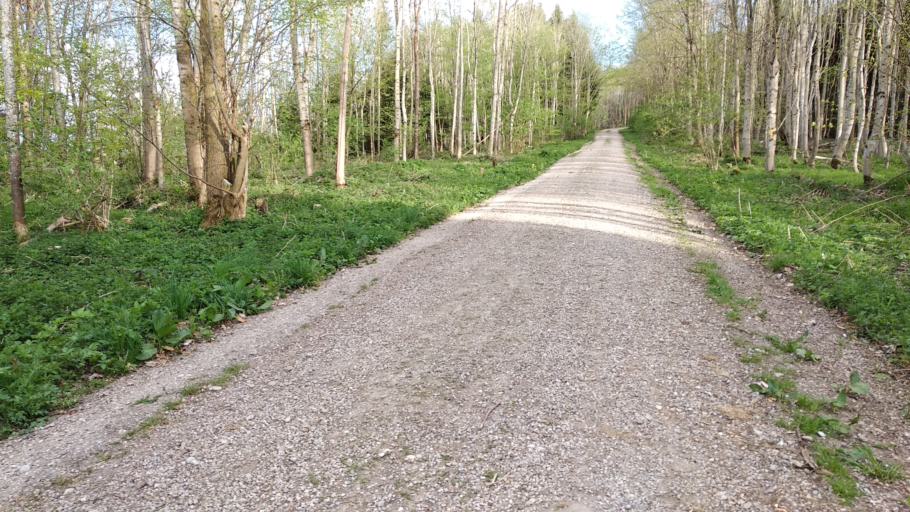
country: DE
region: Bavaria
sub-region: Swabia
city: Woringen
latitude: 47.9353
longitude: 10.1918
